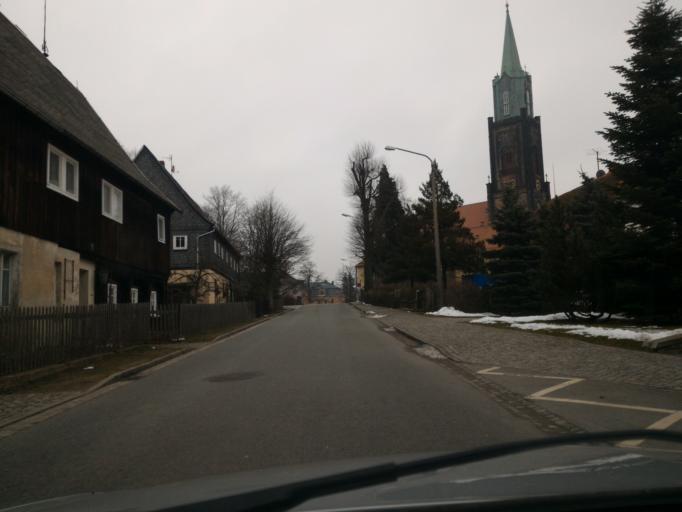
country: DE
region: Saxony
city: Neugersdorf
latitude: 50.9810
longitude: 14.6073
